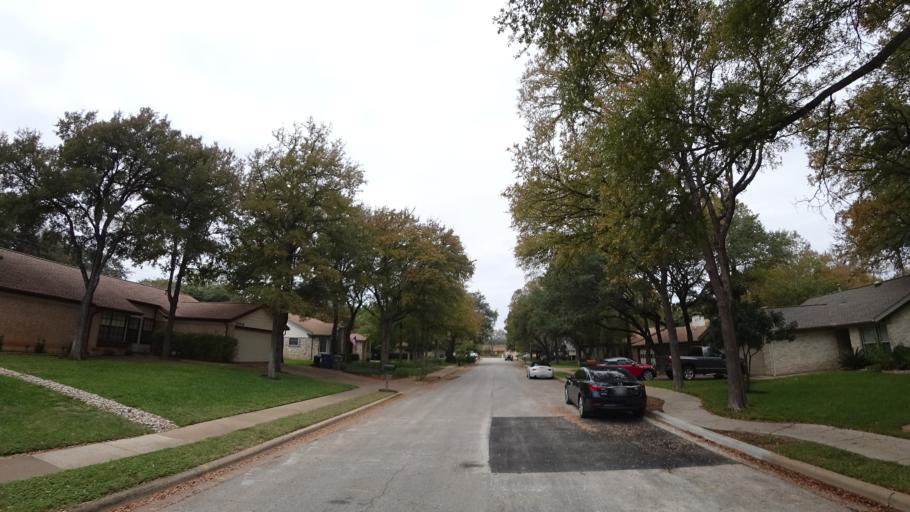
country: US
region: Texas
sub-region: Travis County
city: Wells Branch
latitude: 30.4324
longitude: -97.7165
